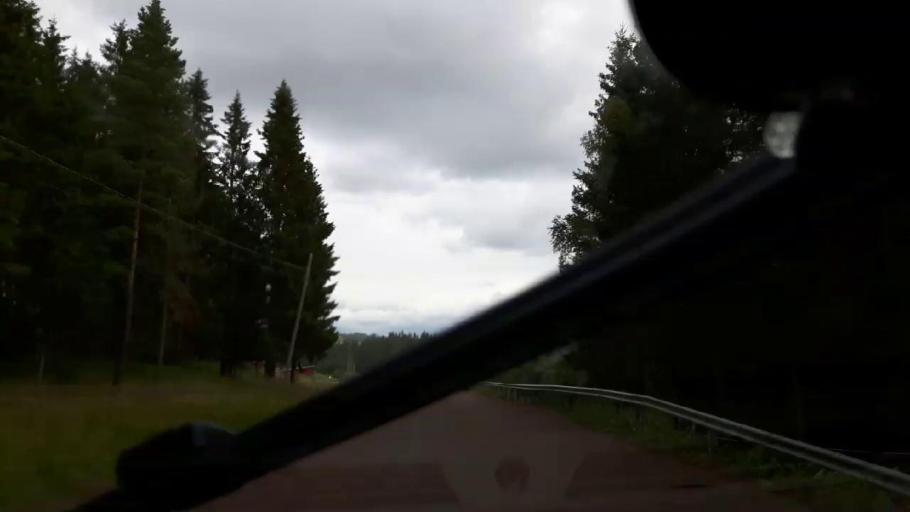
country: SE
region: Jaemtland
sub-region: Krokoms Kommun
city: Valla
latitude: 63.3896
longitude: 13.8621
